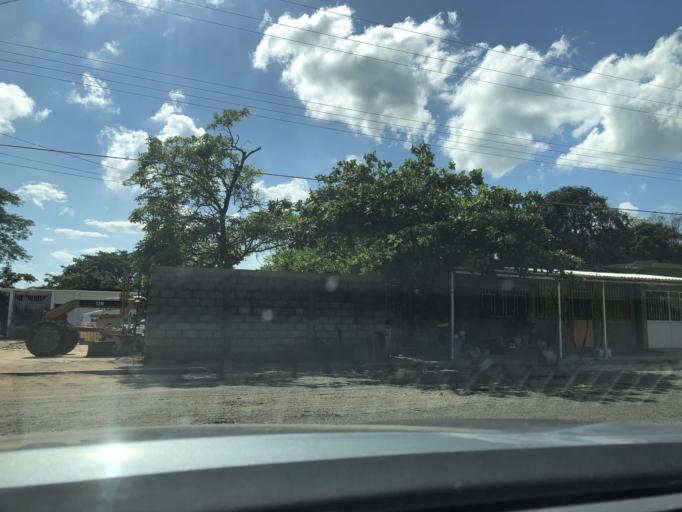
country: MX
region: Oaxaca
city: San Jeronimo Ixtepec
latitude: 16.5574
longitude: -95.1035
